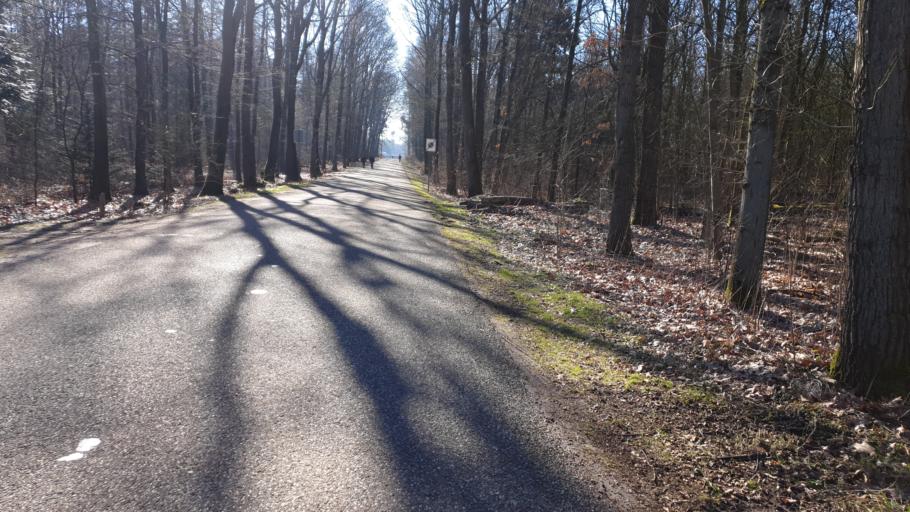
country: NL
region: Gelderland
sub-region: Gemeente Apeldoorn
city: Beekbergen
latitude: 52.1788
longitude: 5.9506
